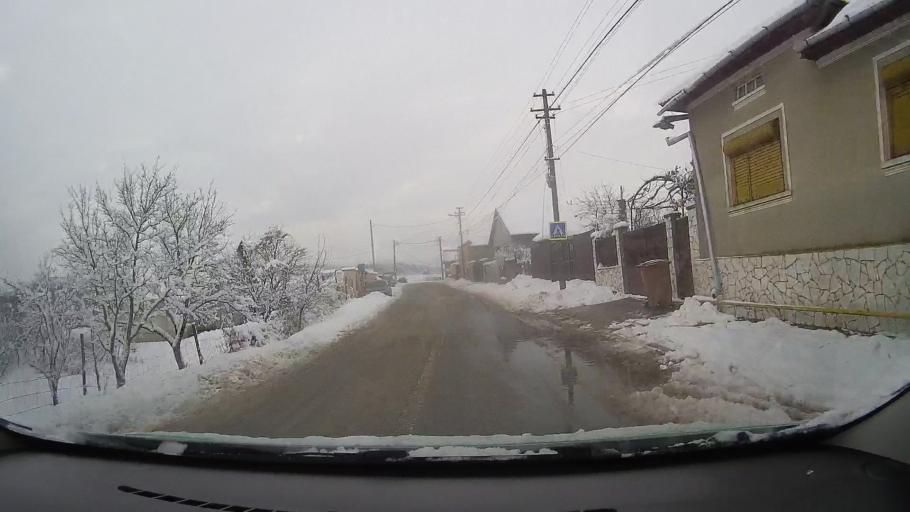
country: RO
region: Alba
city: Vurpar
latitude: 45.9743
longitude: 23.4807
